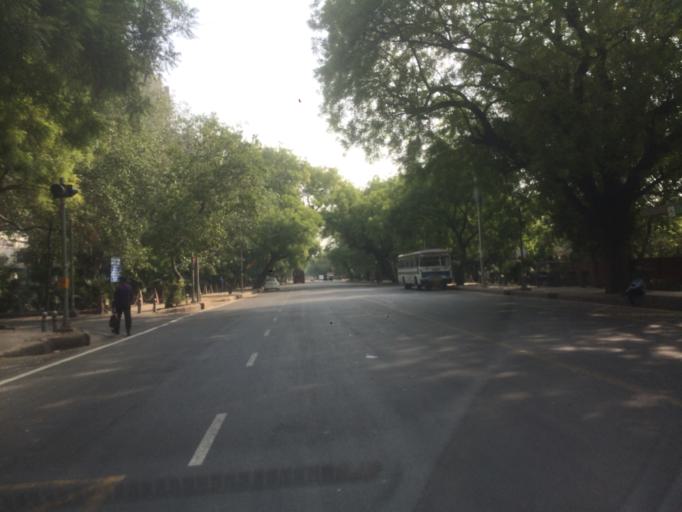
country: IN
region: NCT
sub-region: New Delhi
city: New Delhi
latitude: 28.6253
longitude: 77.2141
